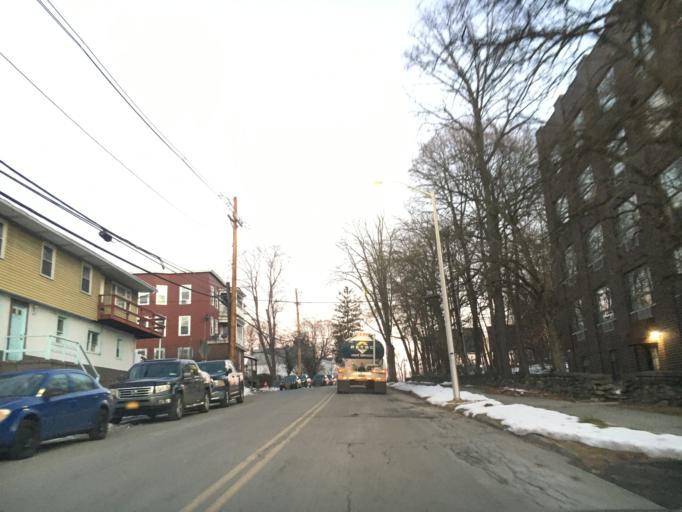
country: US
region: New York
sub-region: Dutchess County
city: Poughkeepsie
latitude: 41.6914
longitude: -73.9317
